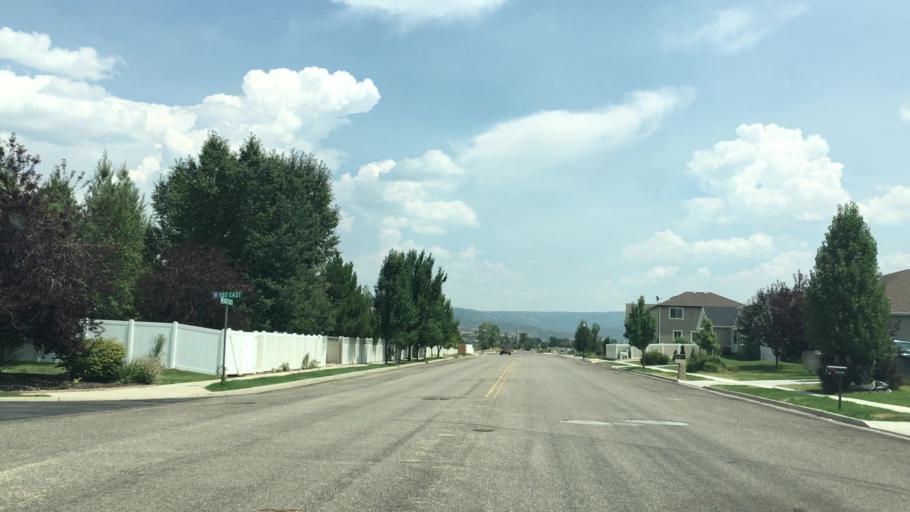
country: US
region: Utah
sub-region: Wasatch County
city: Heber
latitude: 40.5001
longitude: -111.3980
